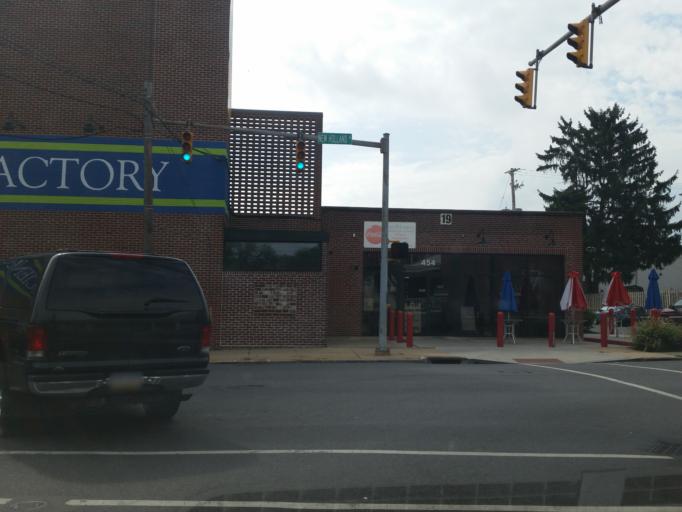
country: US
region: Pennsylvania
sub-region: Lancaster County
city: Lancaster
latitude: 40.0465
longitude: -76.2969
